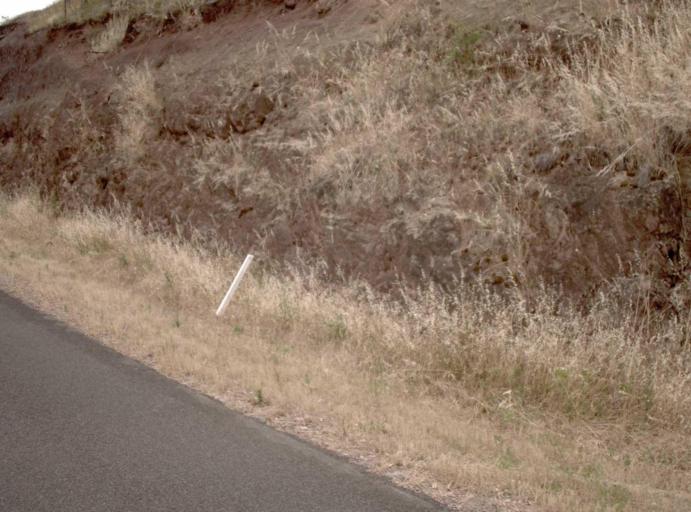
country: AU
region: Victoria
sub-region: Wellington
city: Heyfield
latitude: -37.6661
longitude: 146.6459
